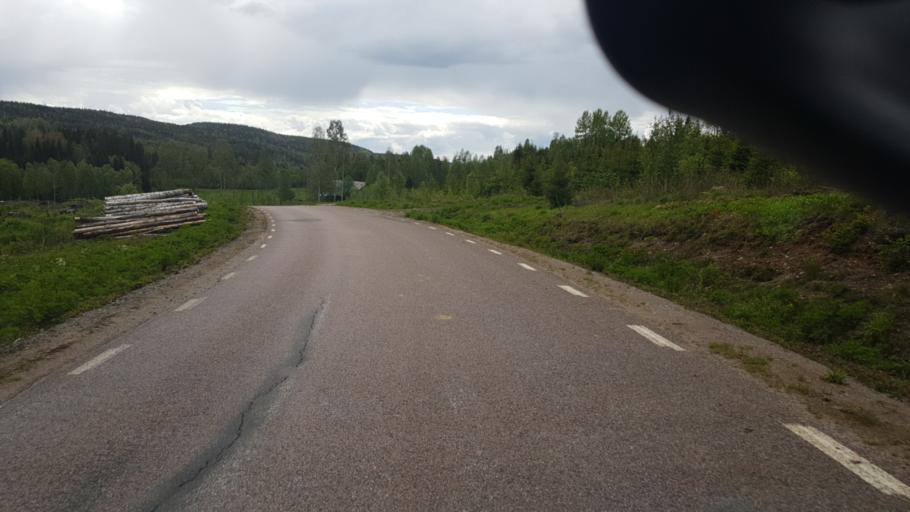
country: SE
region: Vaermland
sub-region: Arvika Kommun
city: Arvika
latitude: 59.7630
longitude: 12.8209
